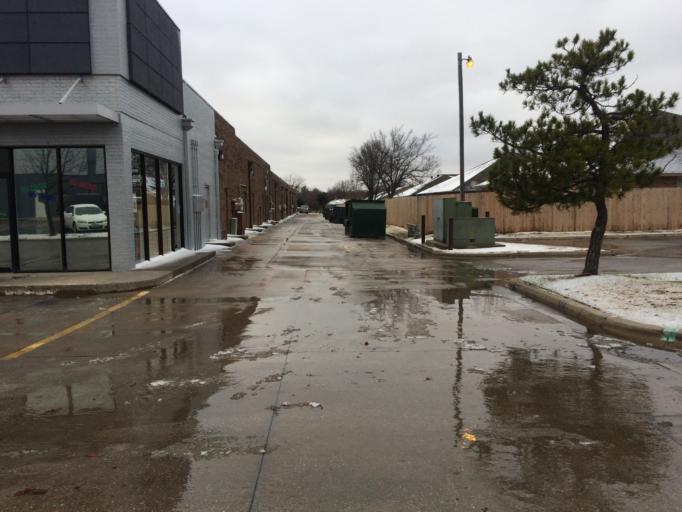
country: US
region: Oklahoma
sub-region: Cleveland County
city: Norman
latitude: 35.2352
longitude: -97.4867
